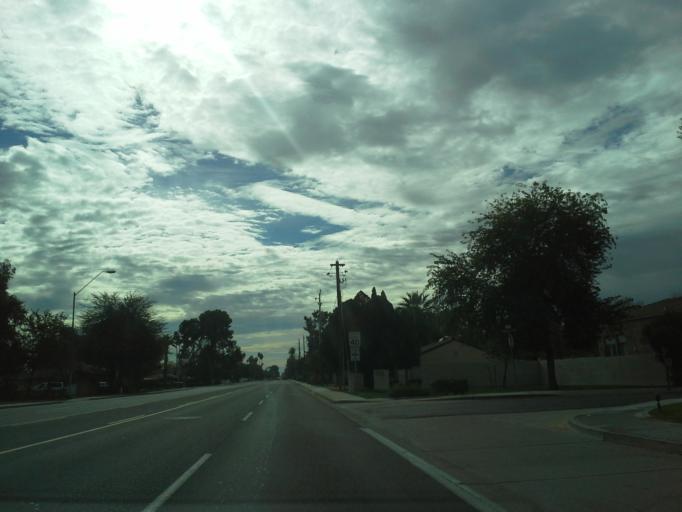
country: US
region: Arizona
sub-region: Maricopa County
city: Glendale
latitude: 33.5663
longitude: -112.0826
